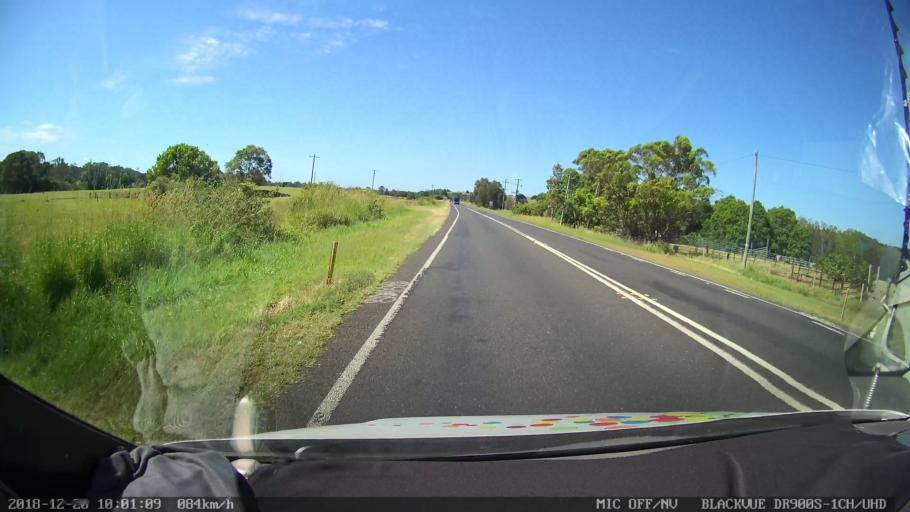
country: AU
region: New South Wales
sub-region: Lismore Municipality
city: Lismore
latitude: -28.8409
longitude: 153.2633
